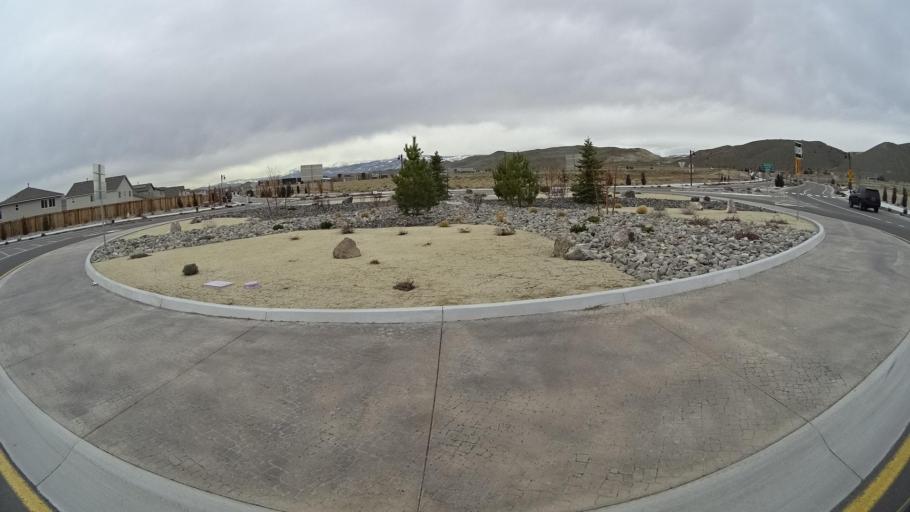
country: US
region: Nevada
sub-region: Washoe County
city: Spanish Springs
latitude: 39.6153
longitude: -119.7184
